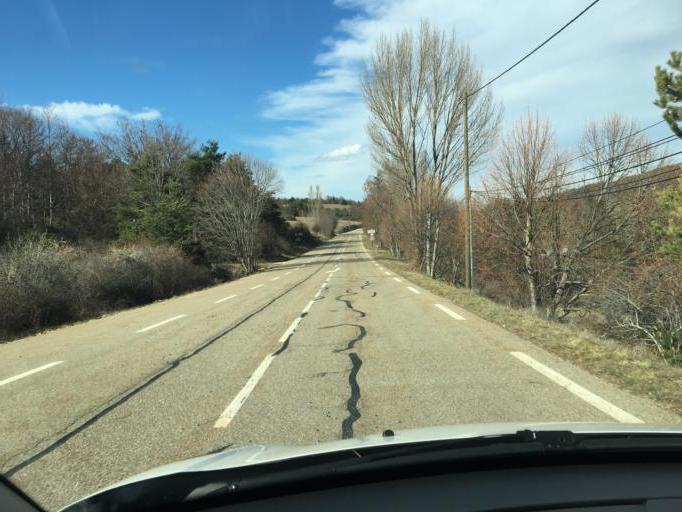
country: FR
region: Provence-Alpes-Cote d'Azur
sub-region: Departement du Vaucluse
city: Saint-Saturnin-les-Apt
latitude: 43.9814
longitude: 5.4723
